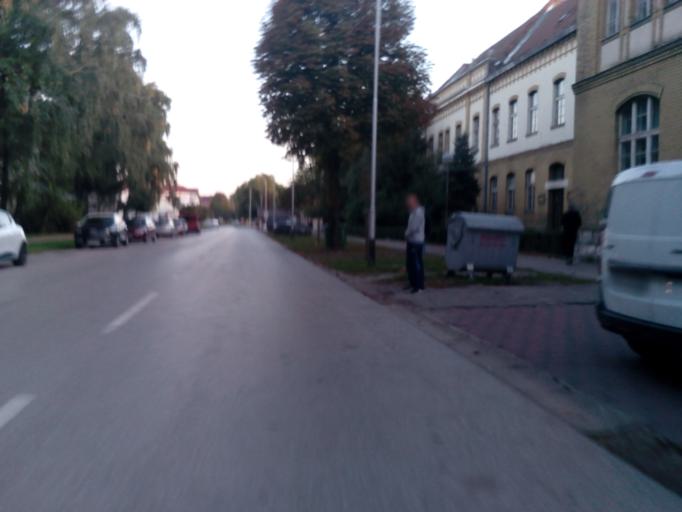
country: HR
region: Vukovarsko-Srijemska
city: Vinkovci
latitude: 45.2981
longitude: 18.8038
